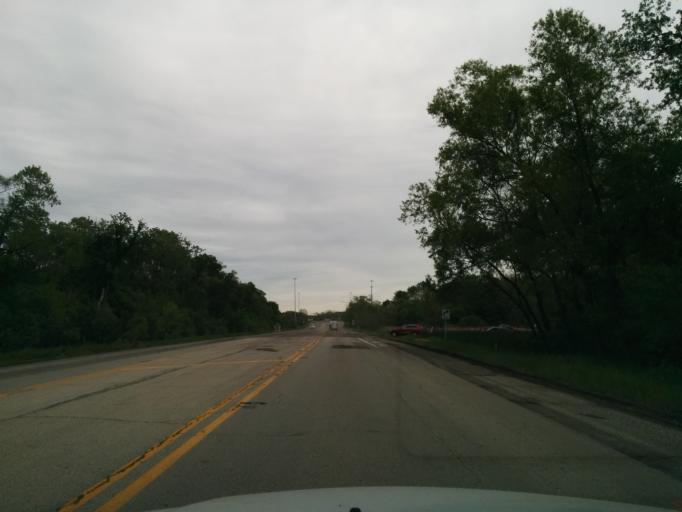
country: US
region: Illinois
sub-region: Cook County
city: Palos Park
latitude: 41.6840
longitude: -87.8624
